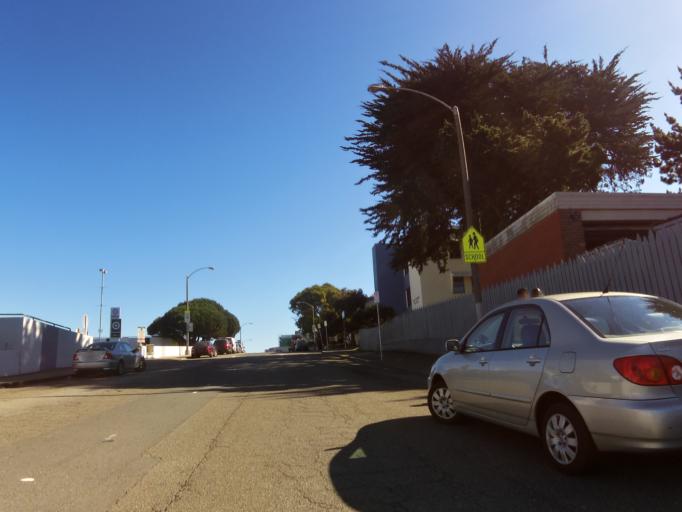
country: US
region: California
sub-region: San Francisco County
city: San Francisco
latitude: 37.7811
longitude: -122.4472
